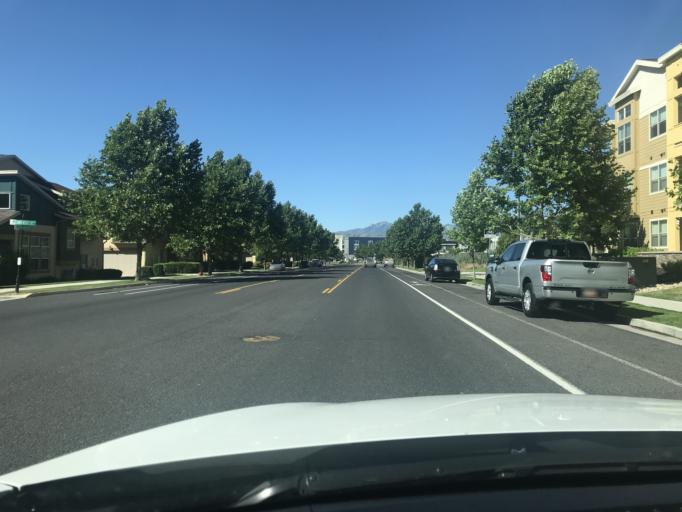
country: US
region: Utah
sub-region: Salt Lake County
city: South Jordan Heights
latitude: 40.5490
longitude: -111.9798
